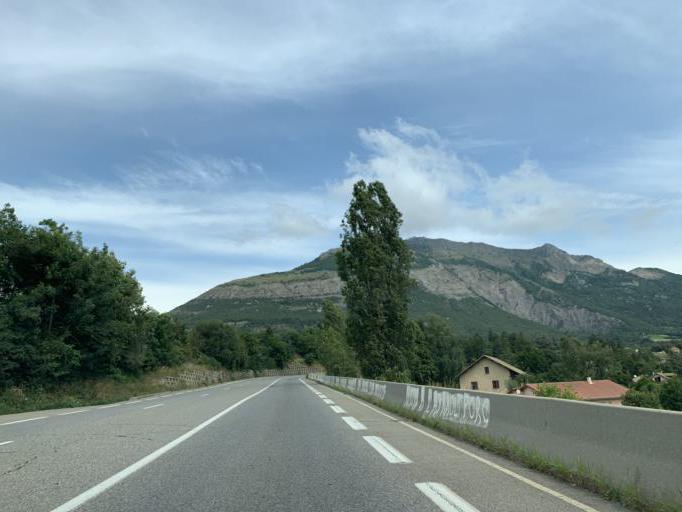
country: FR
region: Provence-Alpes-Cote d'Azur
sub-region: Departement des Hautes-Alpes
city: Gap
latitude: 44.5495
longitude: 6.0368
